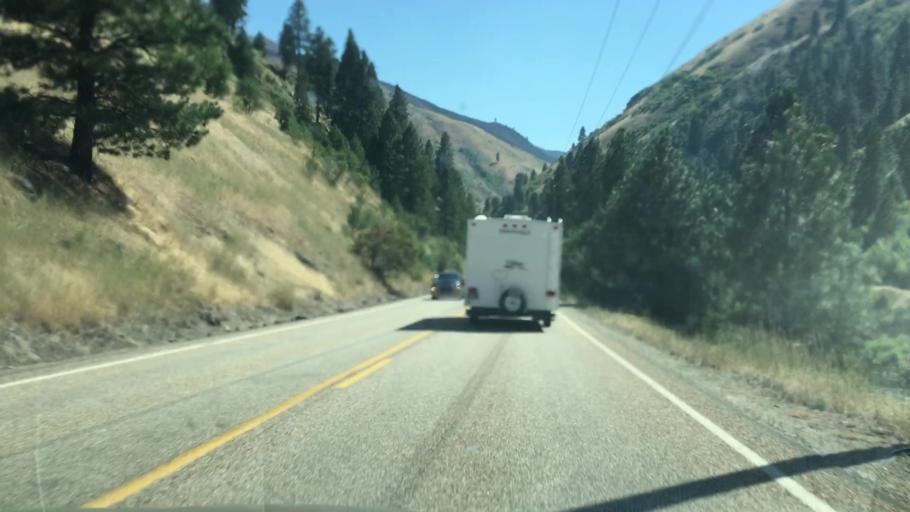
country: US
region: Idaho
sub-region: Boise County
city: Idaho City
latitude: 44.0397
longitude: -116.1326
